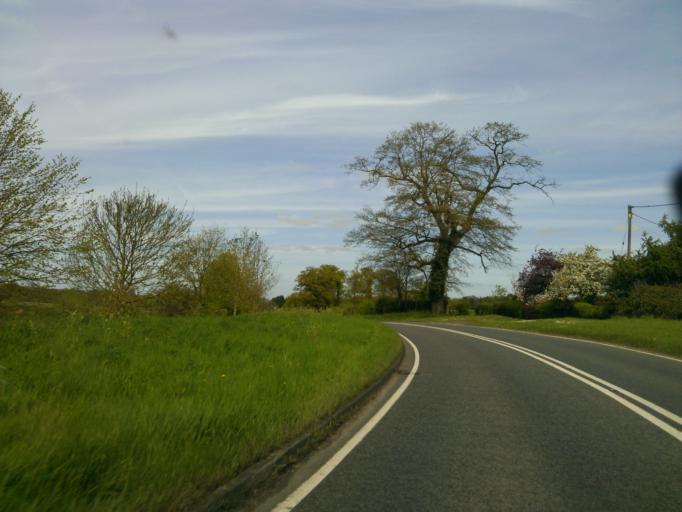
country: GB
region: England
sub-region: Essex
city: Sible Hedingham
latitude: 51.9545
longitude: 0.6317
